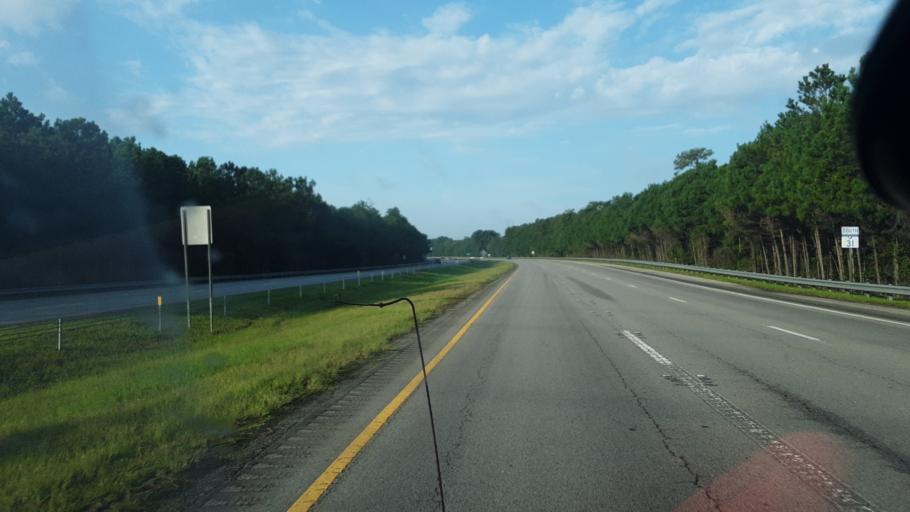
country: US
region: South Carolina
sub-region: Horry County
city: North Myrtle Beach
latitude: 33.8723
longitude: -78.6868
